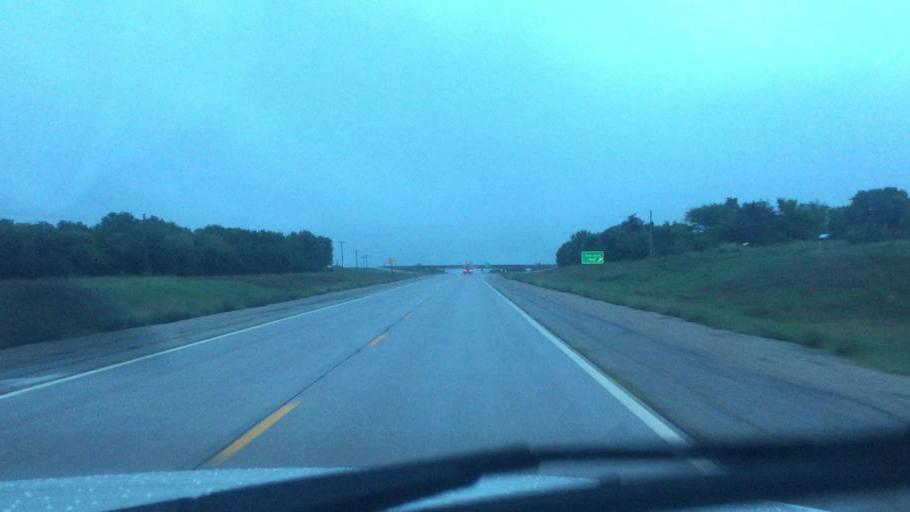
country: US
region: Kansas
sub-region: Allen County
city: Humboldt
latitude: 37.7969
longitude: -95.4114
